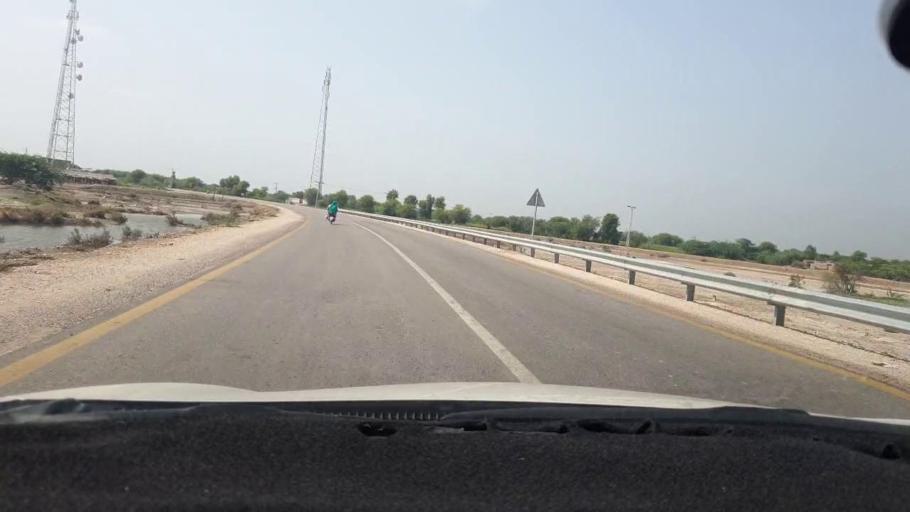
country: PK
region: Sindh
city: Mirpur Khas
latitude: 25.6184
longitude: 69.0841
